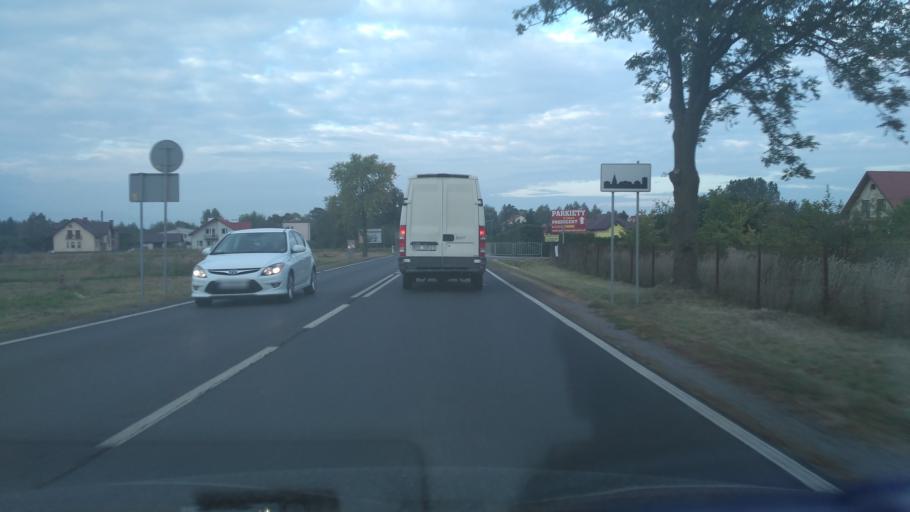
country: PL
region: Lublin Voivodeship
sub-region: Powiat leczynski
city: Spiczyn
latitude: 51.2978
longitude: 22.7186
